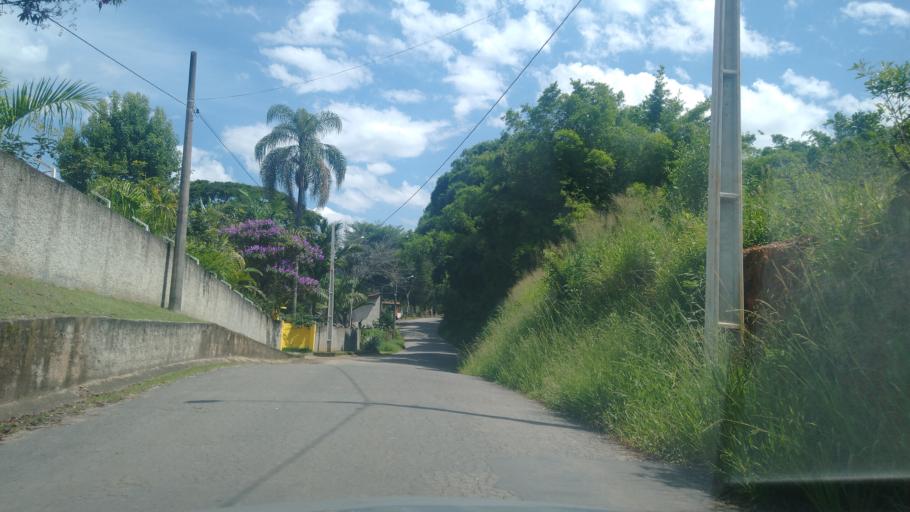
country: BR
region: Minas Gerais
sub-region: Extrema
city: Extrema
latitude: -22.7835
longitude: -46.2873
